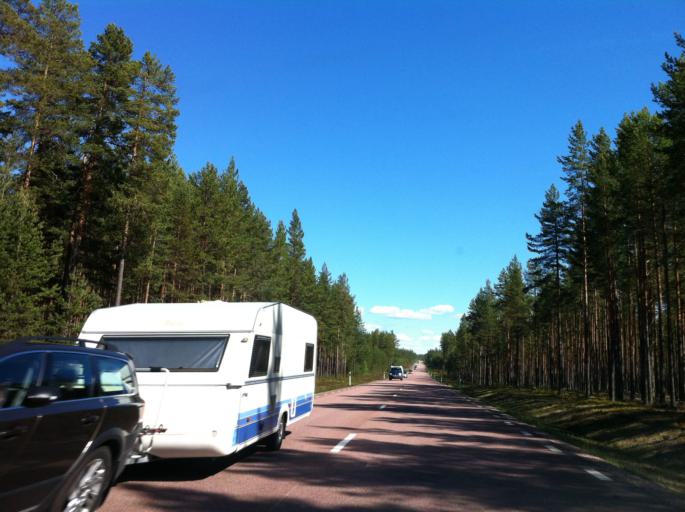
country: SE
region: Dalarna
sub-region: Mora Kommun
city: Mora
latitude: 60.9539
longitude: 14.7320
